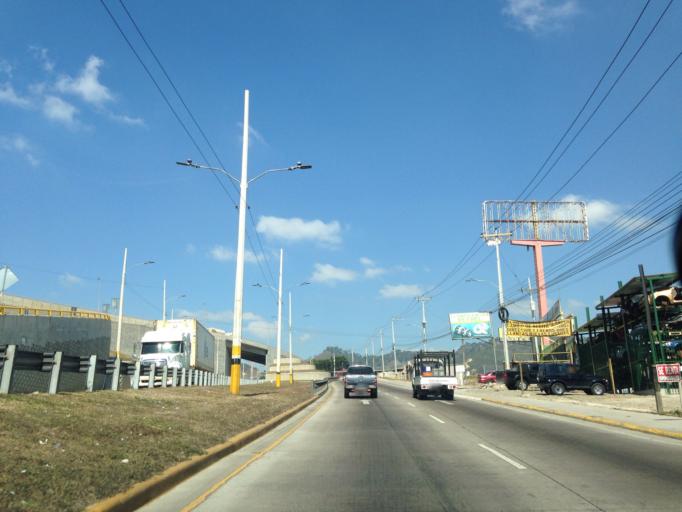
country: HN
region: Francisco Morazan
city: El Lolo
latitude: 14.1122
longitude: -87.2484
